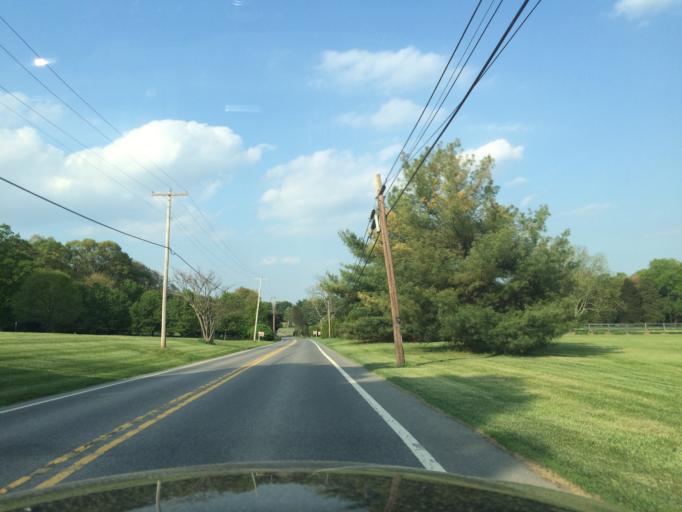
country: US
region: Maryland
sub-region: Carroll County
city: Mount Airy
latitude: 39.3169
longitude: -77.1020
